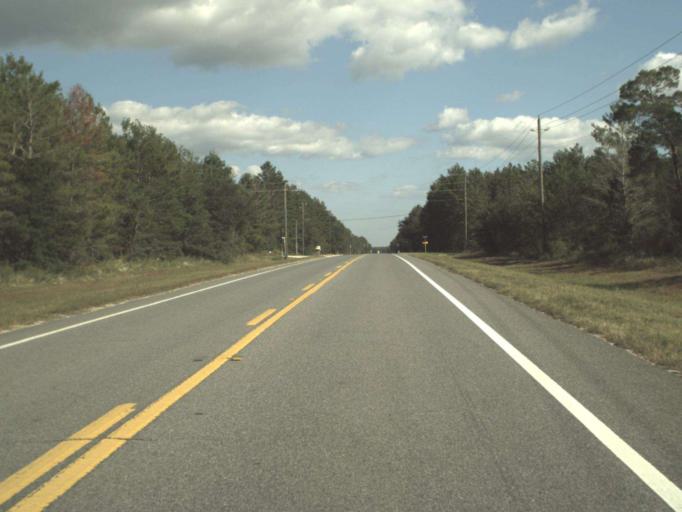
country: US
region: Florida
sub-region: Bay County
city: Lynn Haven
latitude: 30.4290
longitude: -85.6786
